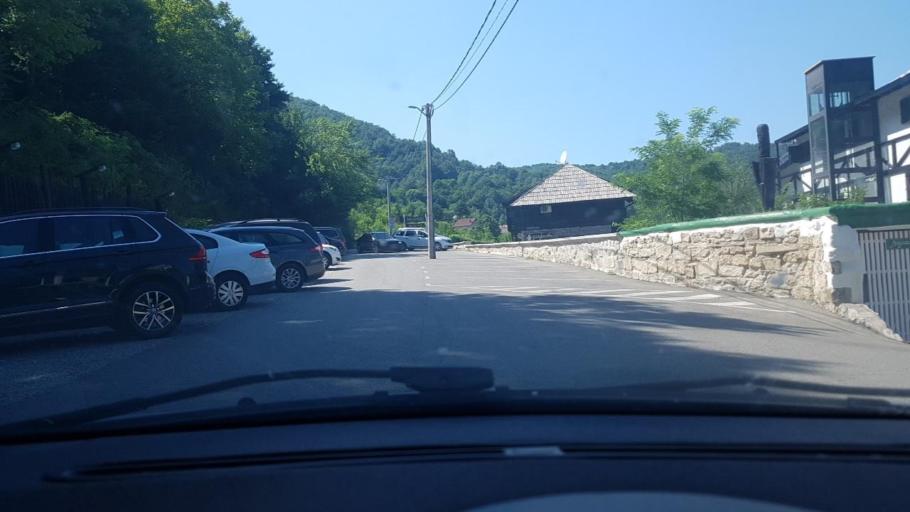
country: BA
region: Federation of Bosnia and Herzegovina
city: Bihac
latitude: 44.7339
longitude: 15.9257
